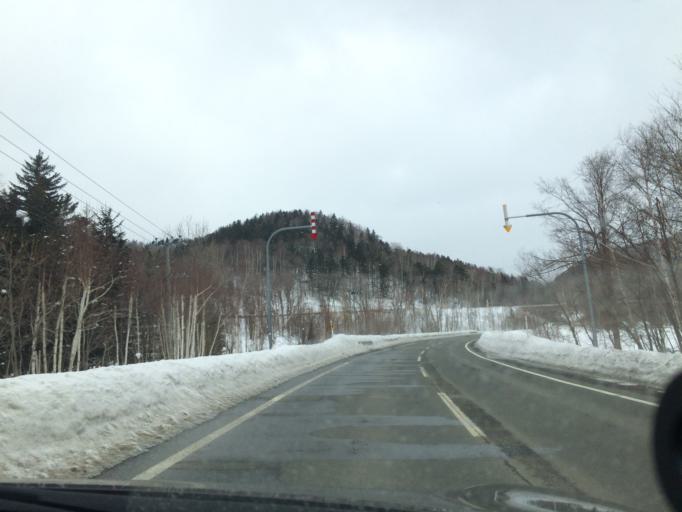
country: JP
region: Hokkaido
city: Shimo-furano
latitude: 43.0590
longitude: 142.5304
